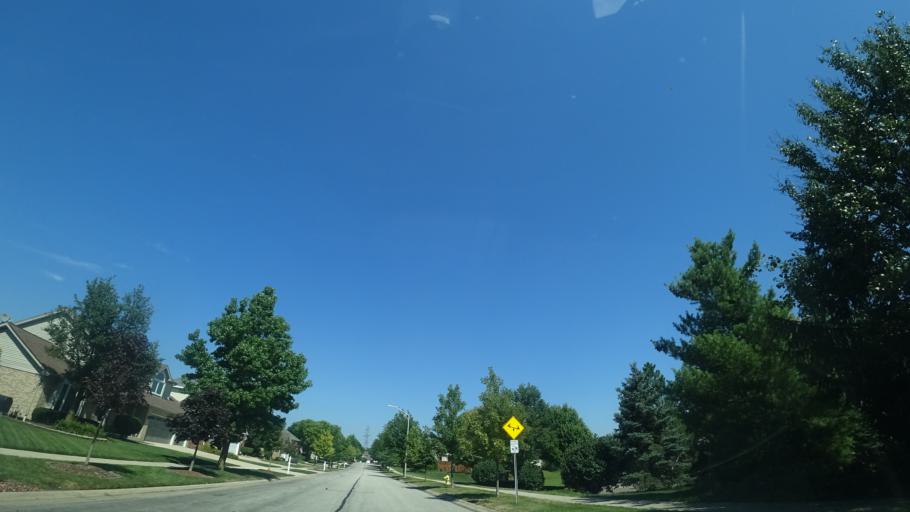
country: US
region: Illinois
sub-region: Will County
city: Mokena
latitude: 41.5710
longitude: -87.9009
